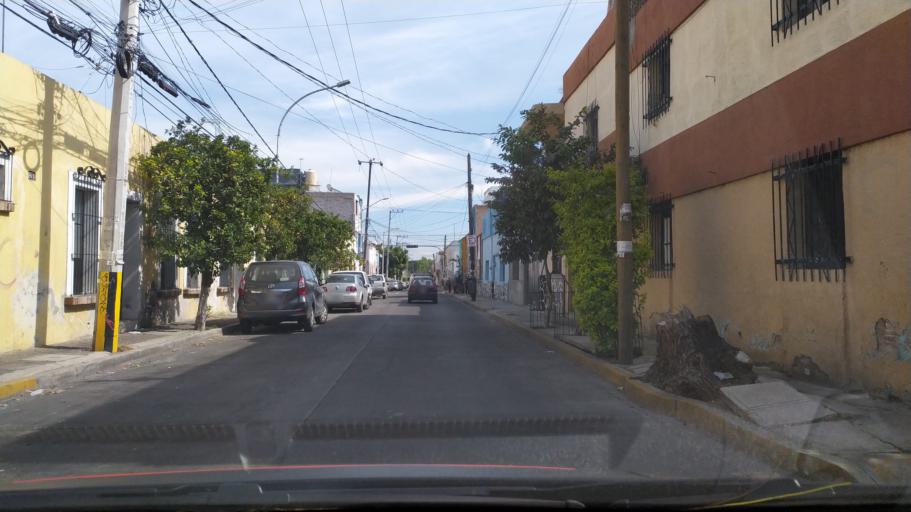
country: MX
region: Jalisco
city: Guadalajara
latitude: 20.6821
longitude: -103.3352
